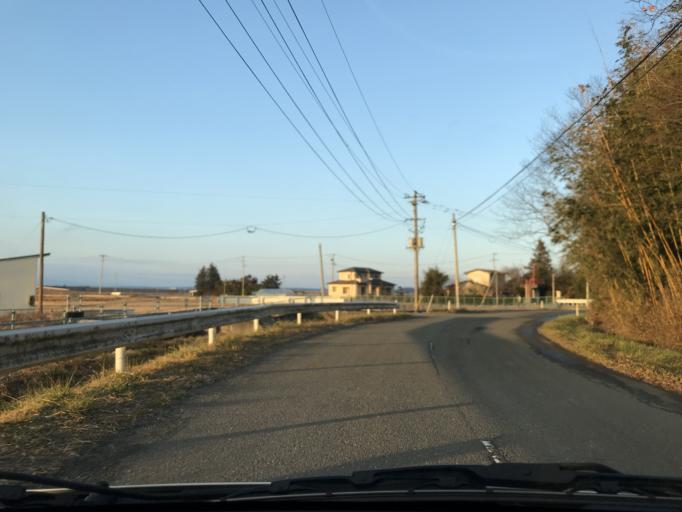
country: JP
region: Miyagi
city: Wakuya
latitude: 38.7077
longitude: 141.1567
